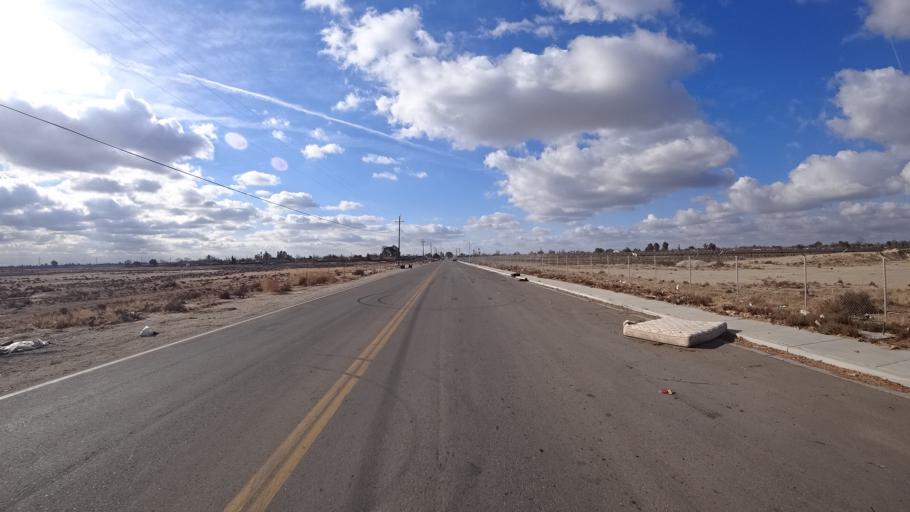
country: US
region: California
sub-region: Kern County
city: Greenfield
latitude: 35.3250
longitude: -118.9767
